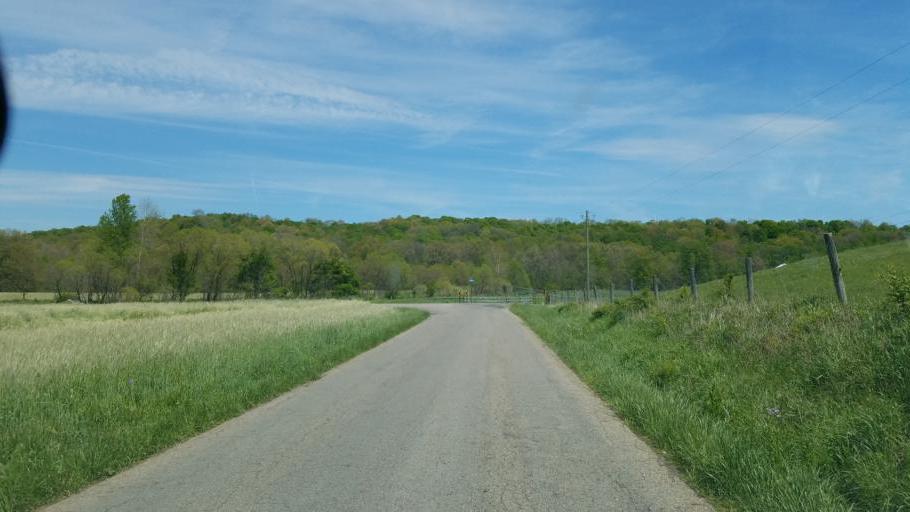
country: US
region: Ohio
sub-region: Knox County
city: Gambier
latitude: 40.4243
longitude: -82.3866
